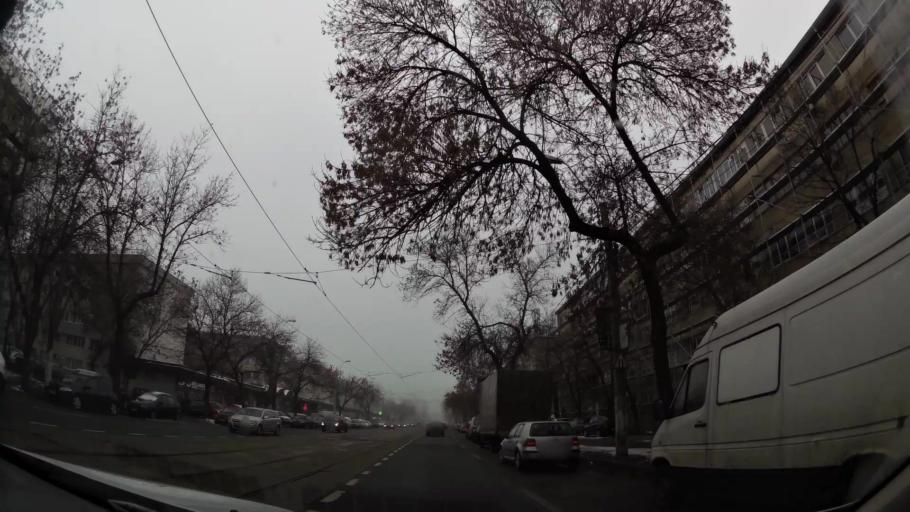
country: RO
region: Ilfov
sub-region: Comuna Chiajna
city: Rosu
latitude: 44.4623
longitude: 26.0435
